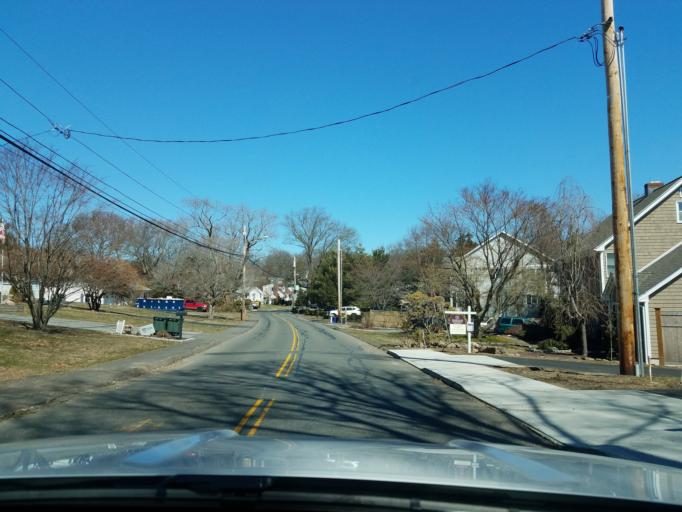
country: US
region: Connecticut
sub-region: Fairfield County
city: Fairfield
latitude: 41.1825
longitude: -73.2576
